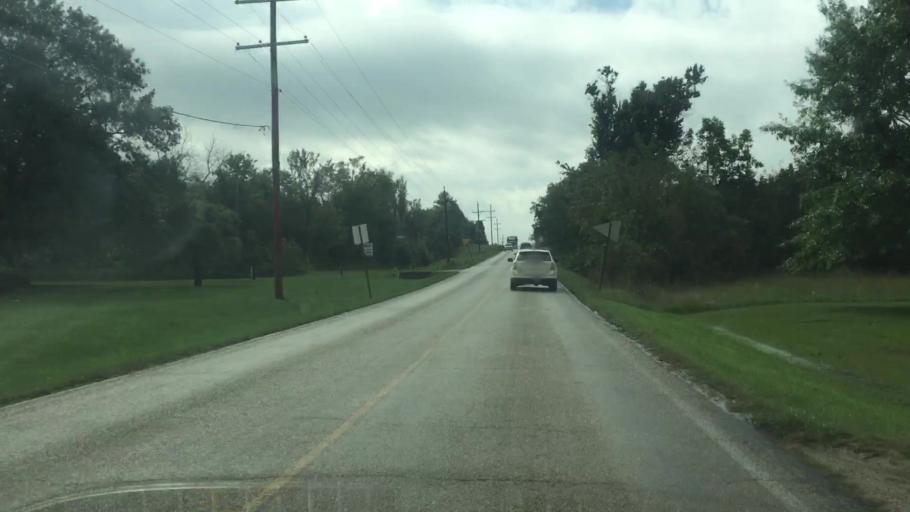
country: US
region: Kansas
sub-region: Allen County
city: Humboldt
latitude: 37.8644
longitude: -95.4369
